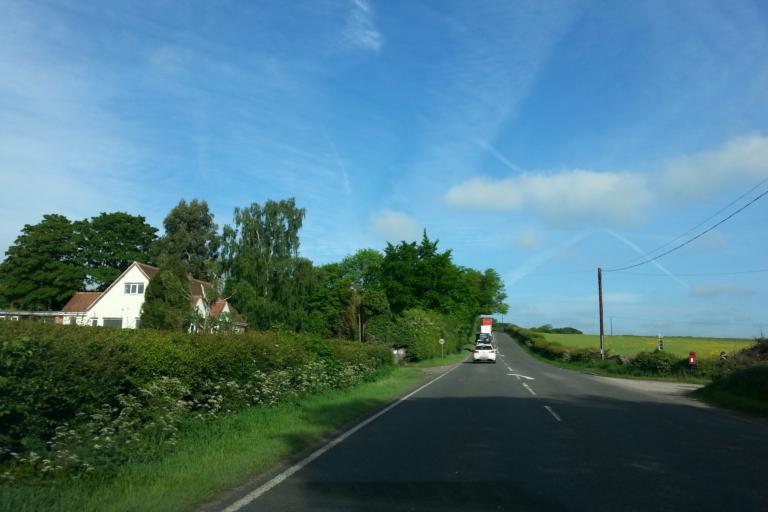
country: GB
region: England
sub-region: Nottinghamshire
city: Southwell
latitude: 53.1118
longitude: -0.9689
